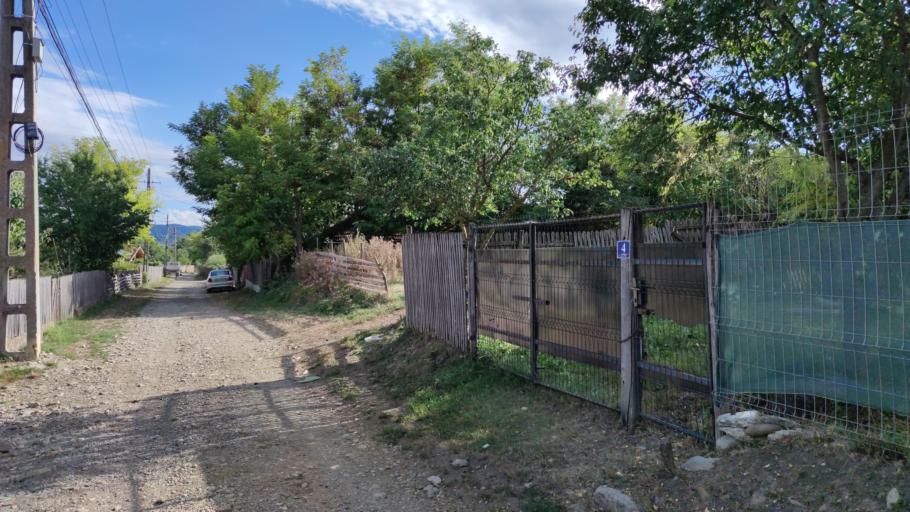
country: RO
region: Buzau
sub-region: Comuna Beceni
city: Valea Parului
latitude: 45.3594
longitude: 26.7647
